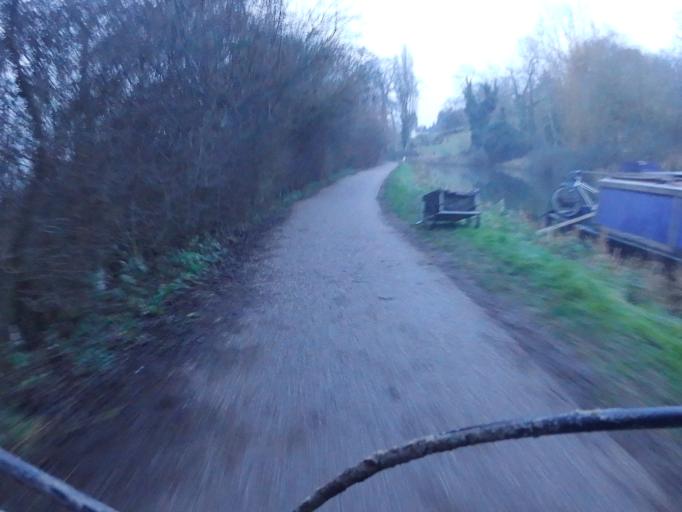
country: GB
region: England
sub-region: Bath and North East Somerset
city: Bath
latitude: 51.3930
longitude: -2.3371
